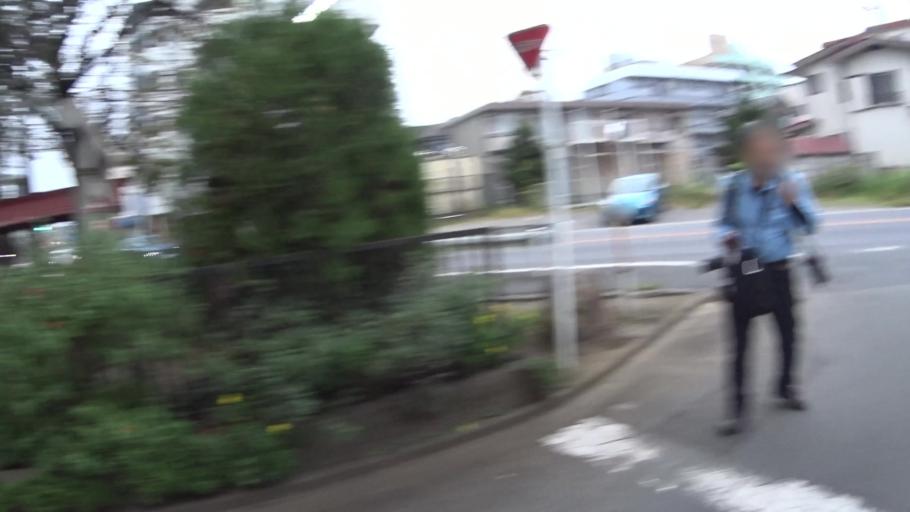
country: JP
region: Saitama
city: Hanno
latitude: 35.8525
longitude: 139.3133
